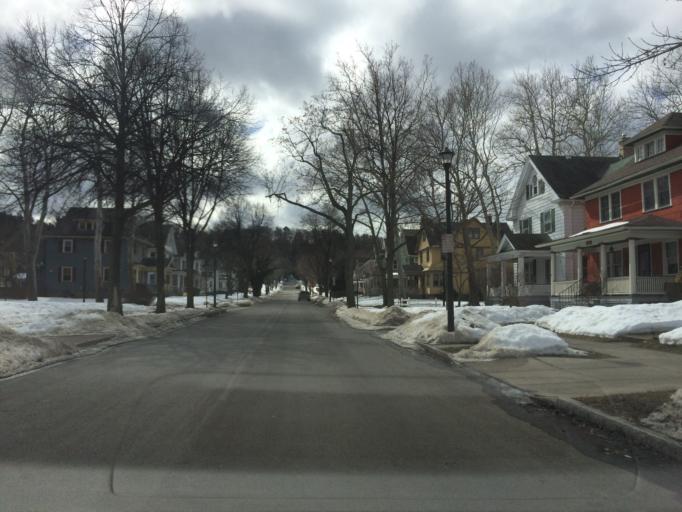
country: US
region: New York
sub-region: Monroe County
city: Rochester
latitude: 43.1371
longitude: -77.6009
